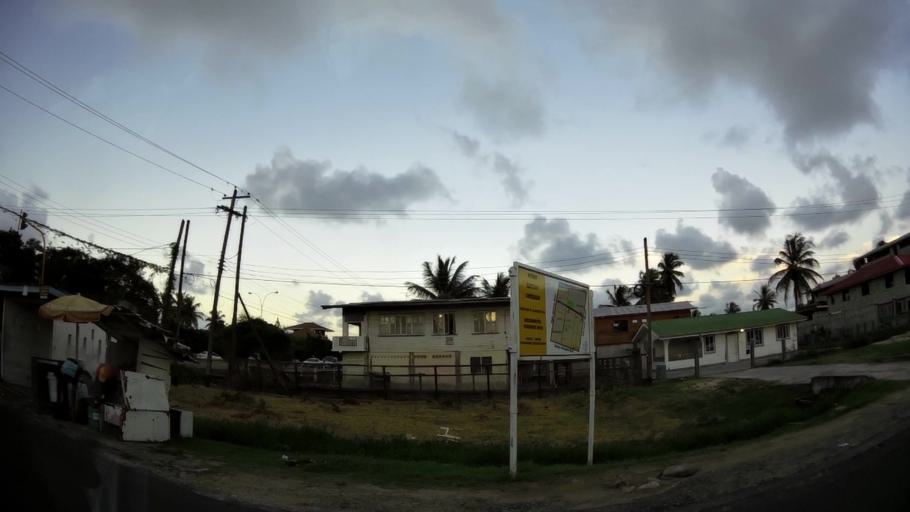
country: GY
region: Demerara-Mahaica
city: Georgetown
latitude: 6.8210
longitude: -58.0974
